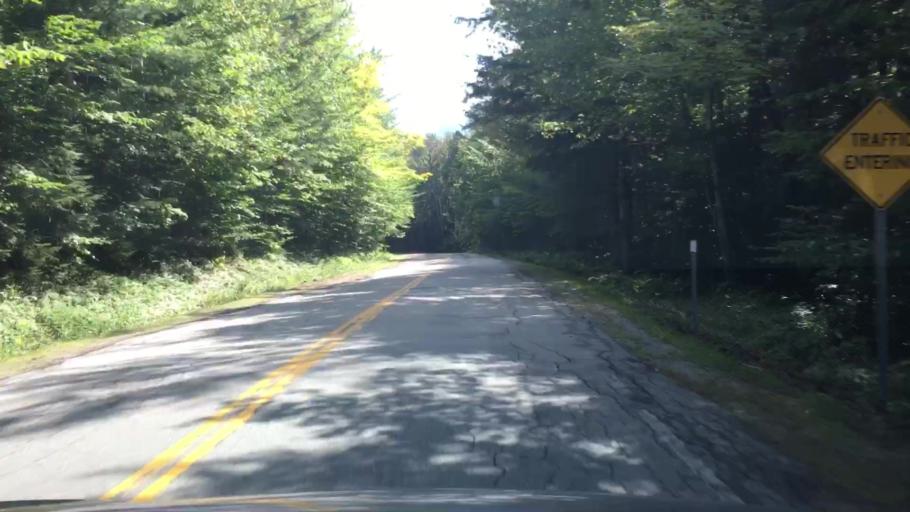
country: US
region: New Hampshire
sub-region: Carroll County
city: Tamworth
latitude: 44.0020
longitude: -71.3215
